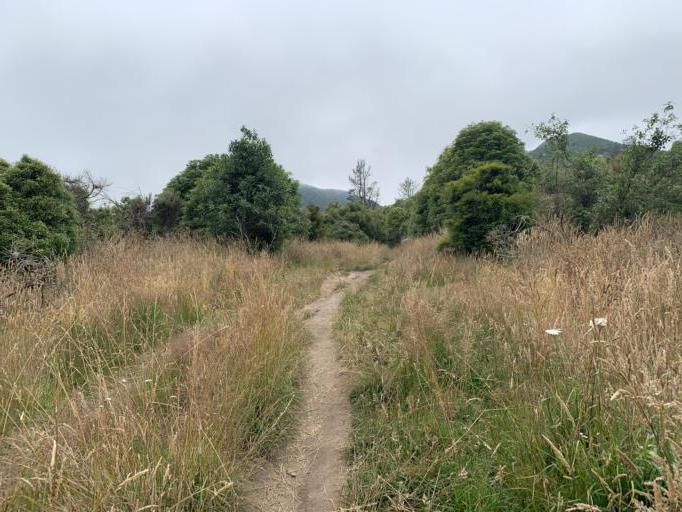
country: NZ
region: Waikato
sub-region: Taupo District
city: Taupo
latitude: -38.6984
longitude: 176.1452
